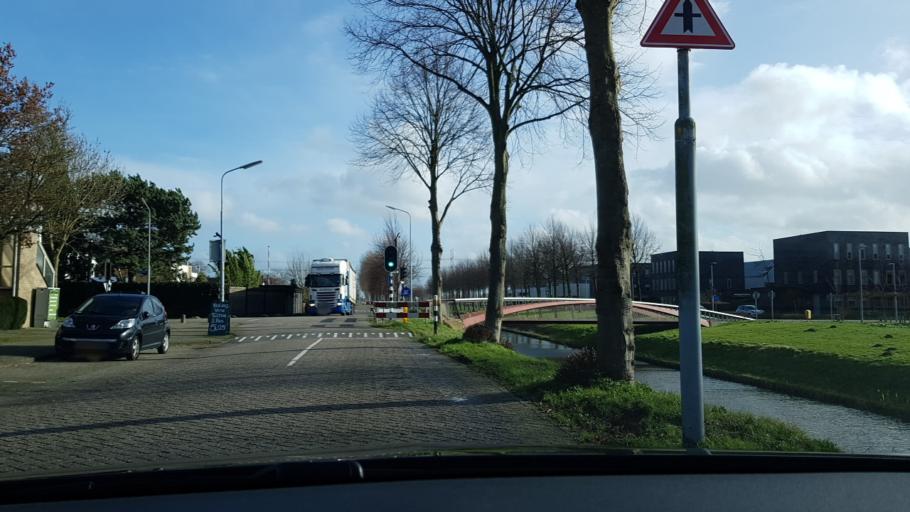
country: NL
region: North Holland
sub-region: Gemeente Haarlemmermeer
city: Hoofddorp
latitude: 52.3488
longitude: 4.6796
